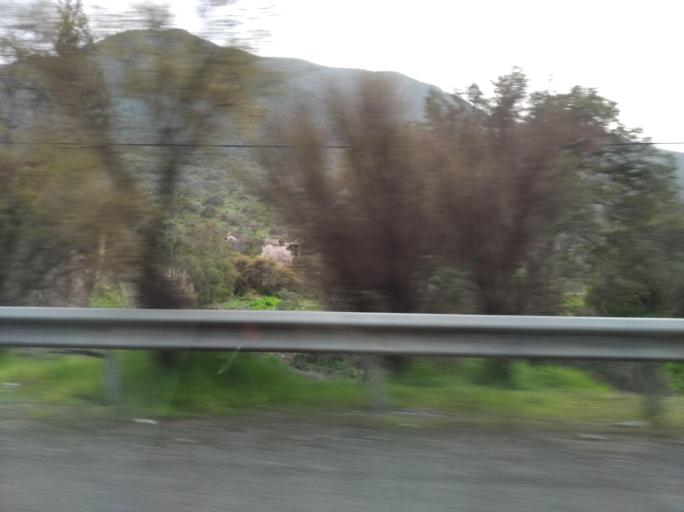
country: CL
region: Santiago Metropolitan
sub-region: Provincia de Chacabuco
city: Lampa
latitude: -33.0770
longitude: -70.9491
